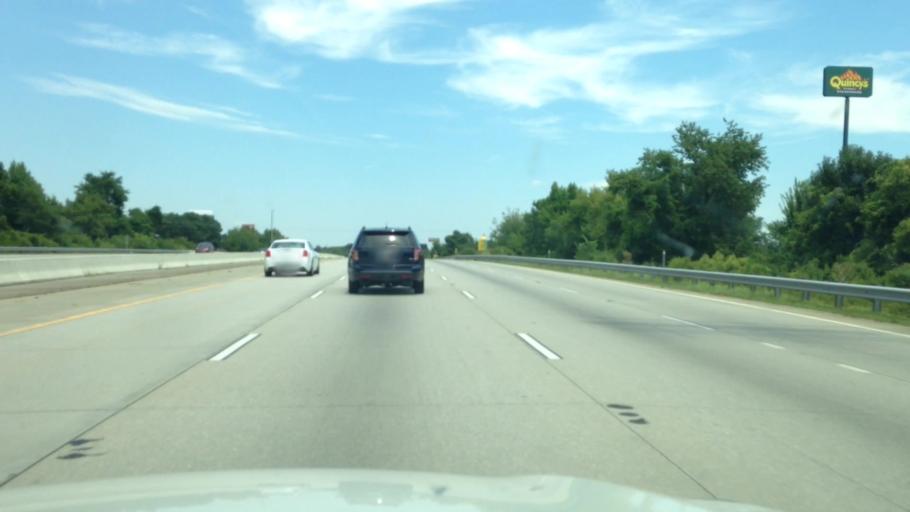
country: US
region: South Carolina
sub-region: Florence County
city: Florence
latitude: 34.2280
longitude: -79.8010
